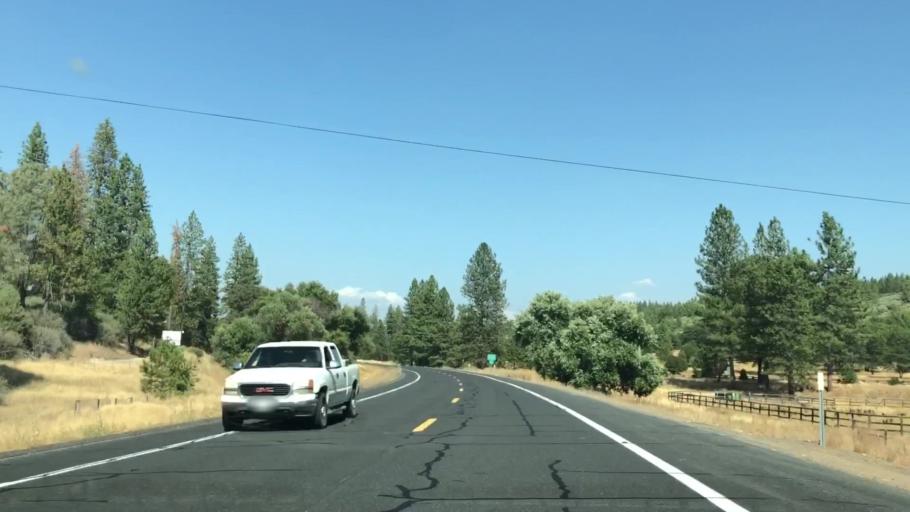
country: US
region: California
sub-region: Tuolumne County
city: Tuolumne City
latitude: 37.8162
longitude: -120.1110
